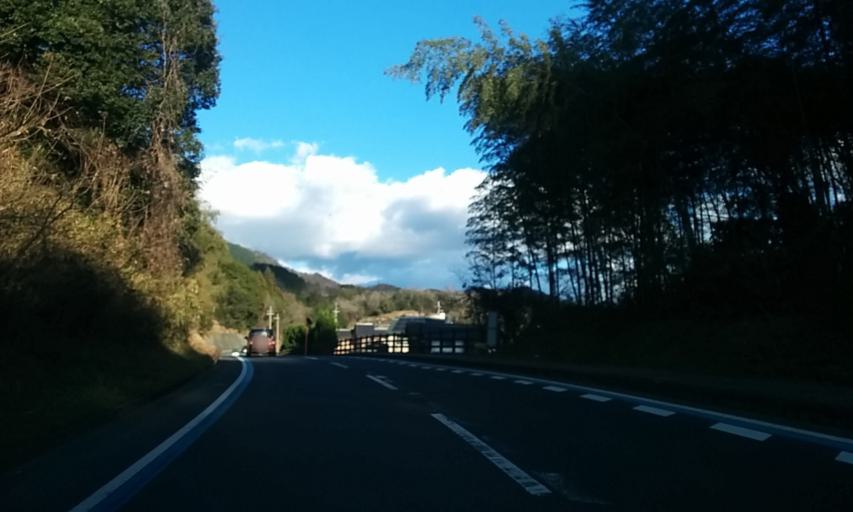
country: JP
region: Kyoto
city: Fukuchiyama
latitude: 35.3162
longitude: 135.1242
